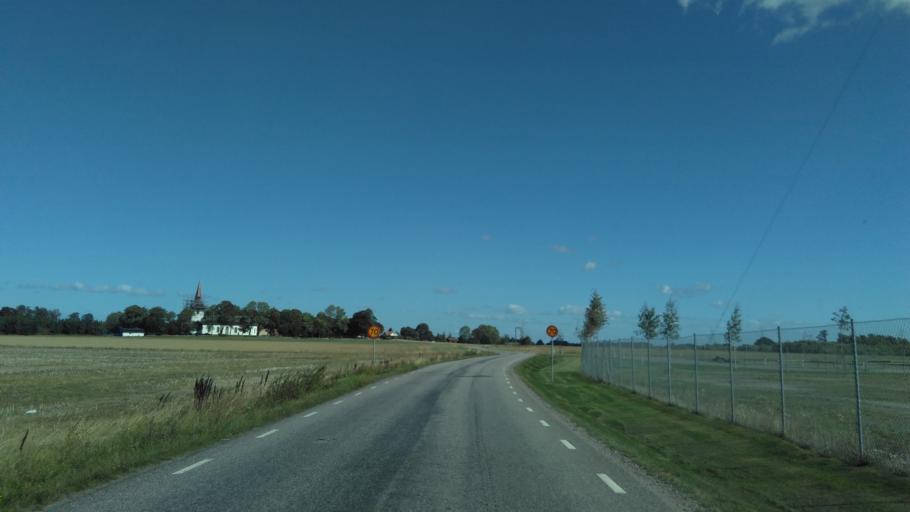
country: SE
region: Vaestra Goetaland
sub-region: Vara Kommun
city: Vara
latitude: 58.2587
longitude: 13.0004
